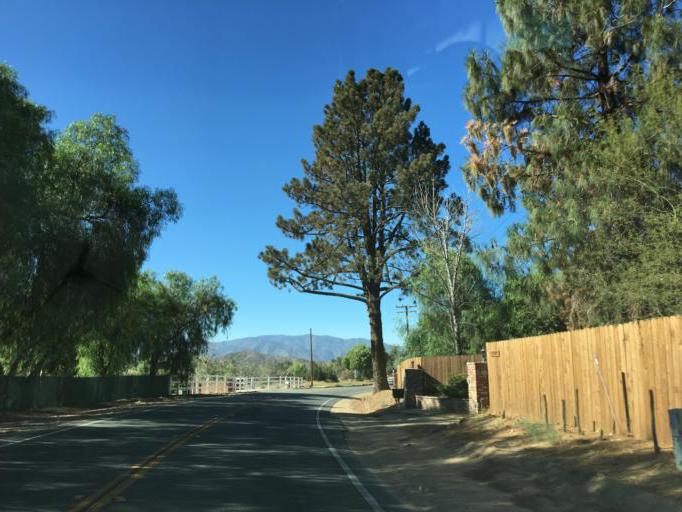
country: US
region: California
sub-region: Los Angeles County
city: Agua Dulce
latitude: 34.5026
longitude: -118.3240
